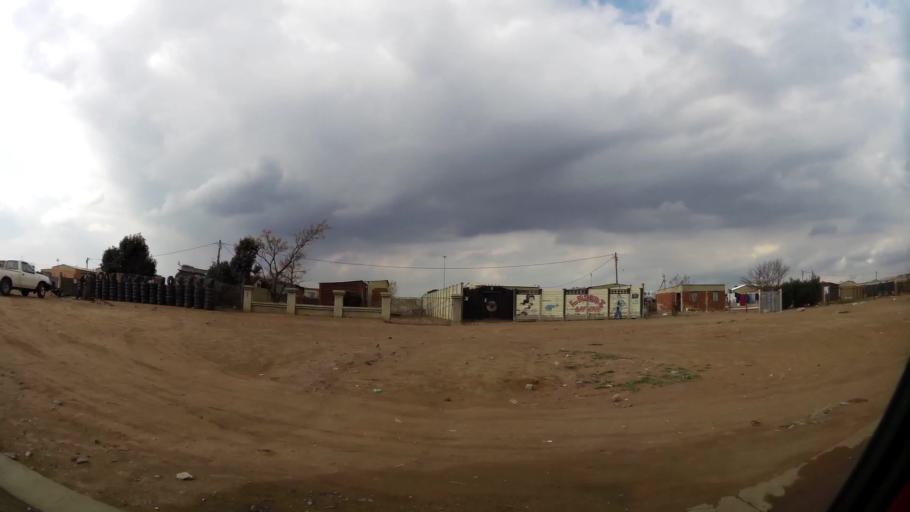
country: ZA
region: Gauteng
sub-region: Sedibeng District Municipality
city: Vanderbijlpark
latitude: -26.6800
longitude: 27.7808
